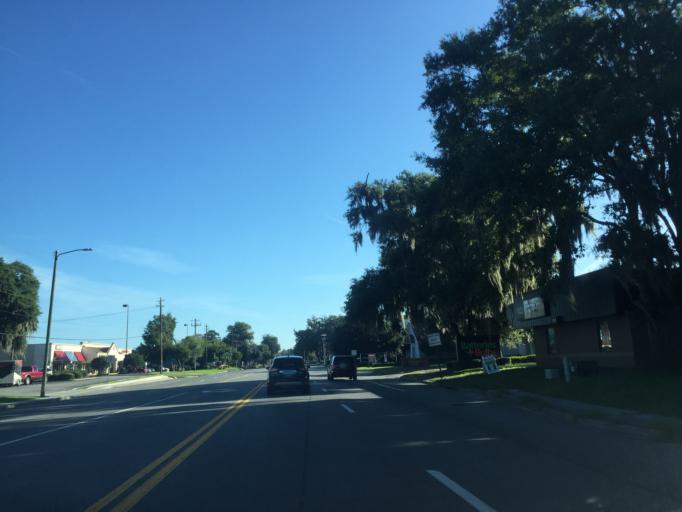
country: US
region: Georgia
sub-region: Chatham County
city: Isle of Hope
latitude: 32.0053
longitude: -81.1105
